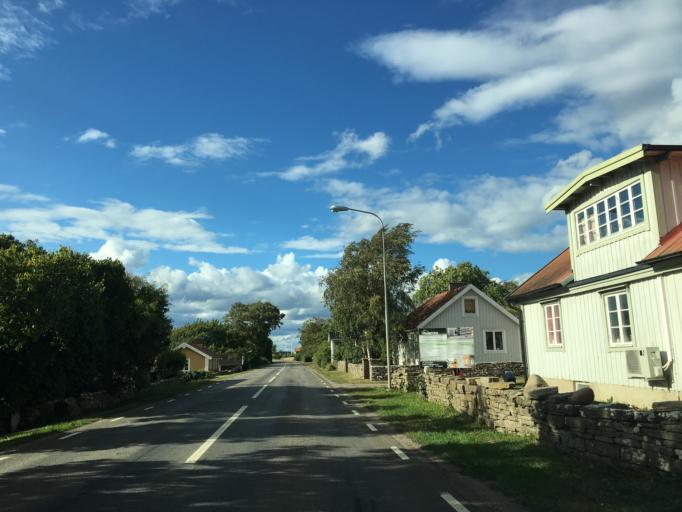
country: SE
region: Kalmar
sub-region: Morbylanga Kommun
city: Moerbylanga
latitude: 56.4819
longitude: 16.4289
